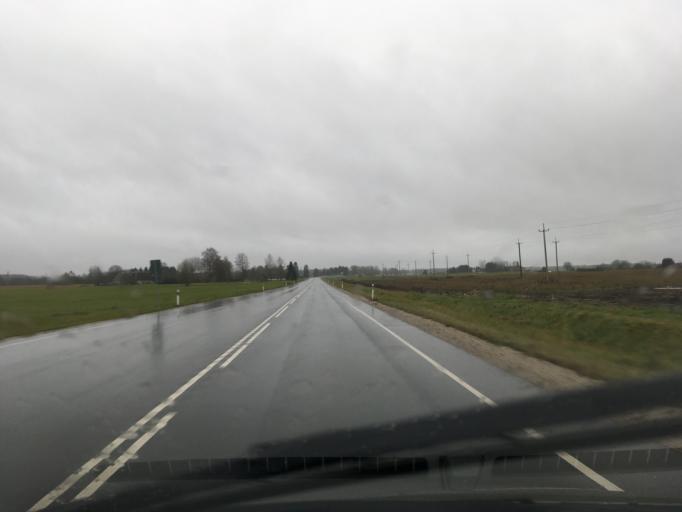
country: EE
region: Harju
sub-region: Nissi vald
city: Turba
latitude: 58.8826
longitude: 24.0889
